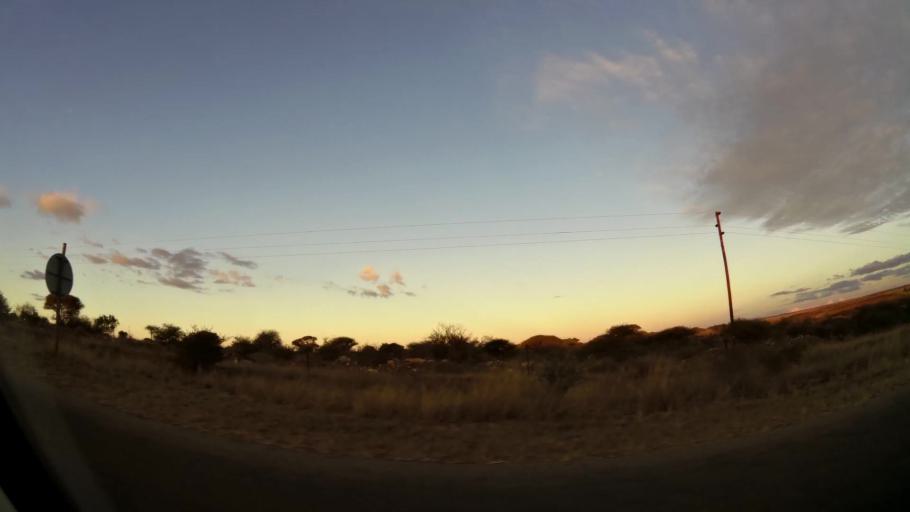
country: ZA
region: Limpopo
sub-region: Capricorn District Municipality
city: Polokwane
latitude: -23.7657
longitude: 29.4746
